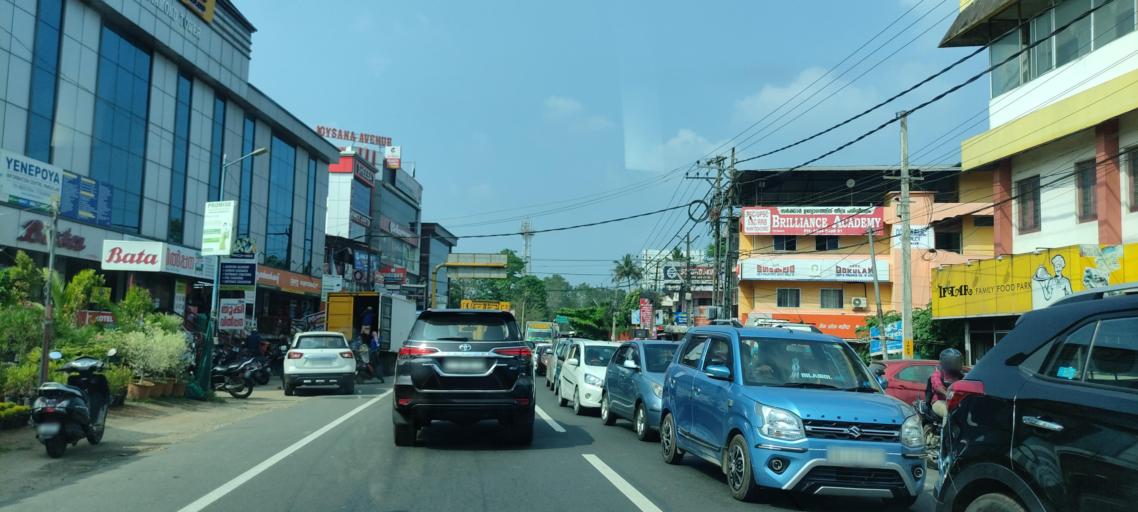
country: IN
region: Kerala
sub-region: Pattanamtitta
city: Adur
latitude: 9.2266
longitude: 76.6781
